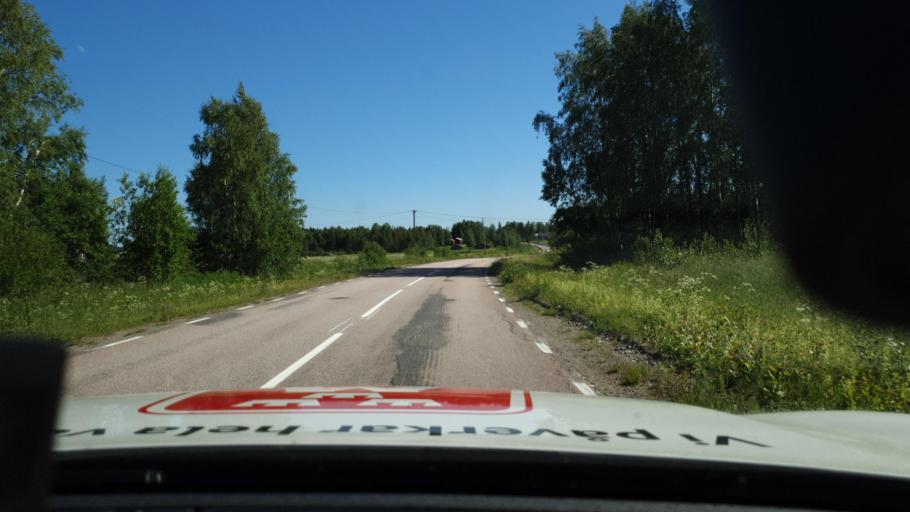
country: SE
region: Norrbotten
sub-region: Lulea Kommun
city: Ranea
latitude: 65.9247
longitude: 22.4380
